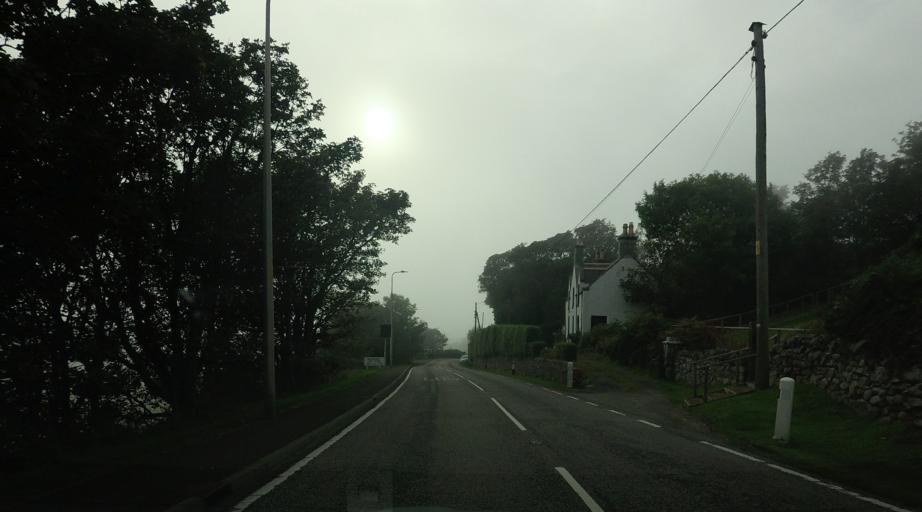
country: GB
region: Scotland
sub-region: Highland
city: Brora
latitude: 58.1184
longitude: -3.6431
